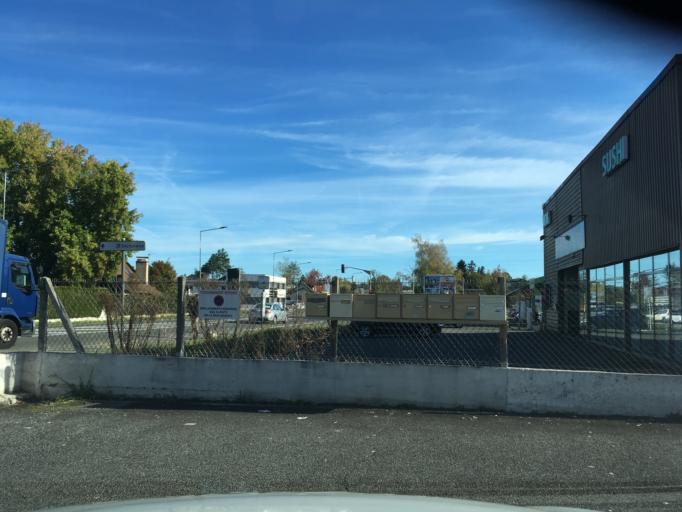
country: FR
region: Aquitaine
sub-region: Departement des Pyrenees-Atlantiques
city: Idron
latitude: 43.3077
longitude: -0.3304
